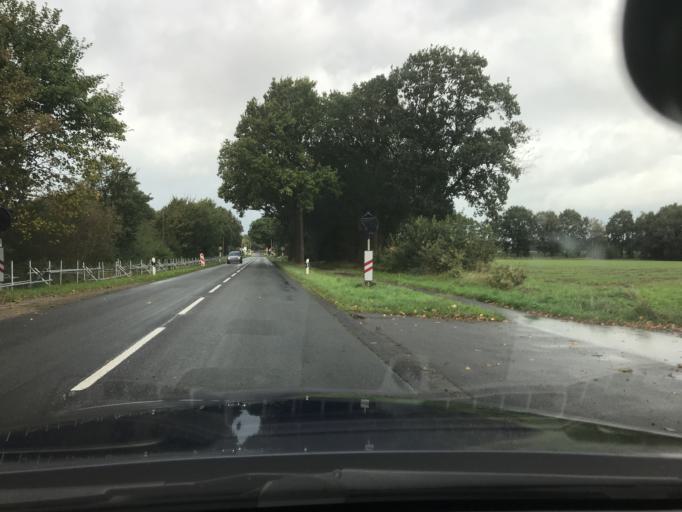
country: DE
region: Lower Saxony
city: Stade
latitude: 53.5675
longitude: 9.4730
